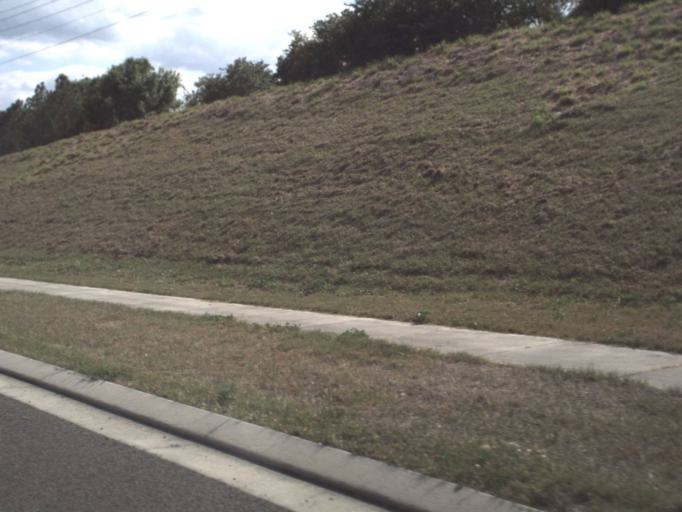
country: US
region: Florida
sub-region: Lake County
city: Clermont
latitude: 28.5093
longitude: -81.7229
